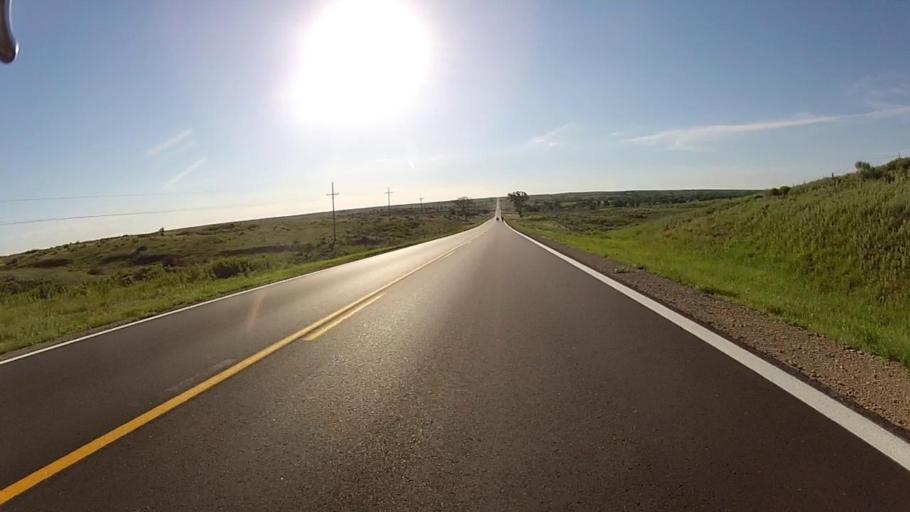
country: US
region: Kansas
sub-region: Comanche County
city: Coldwater
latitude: 37.2814
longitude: -99.0538
